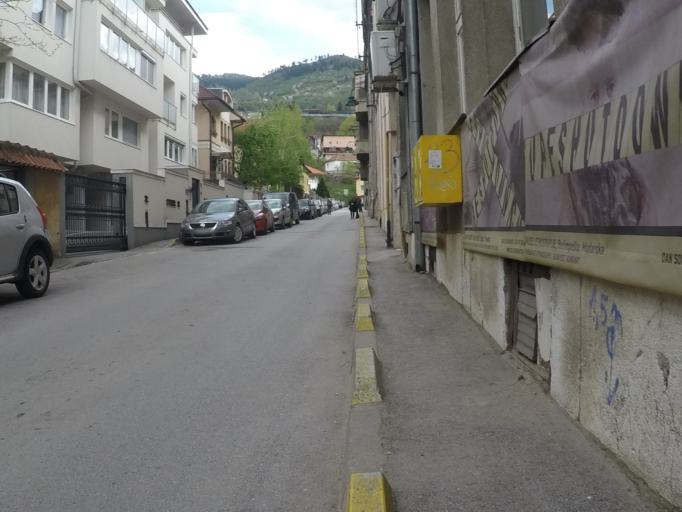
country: BA
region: Federation of Bosnia and Herzegovina
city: Kobilja Glava
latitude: 43.8577
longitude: 18.4340
